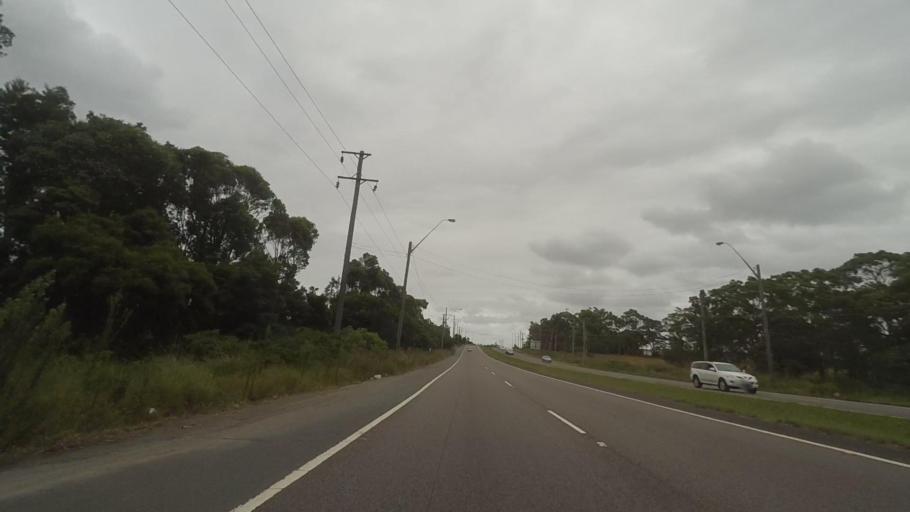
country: AU
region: New South Wales
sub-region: Wyong Shire
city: Buff Point
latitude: -33.2008
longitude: 151.5218
